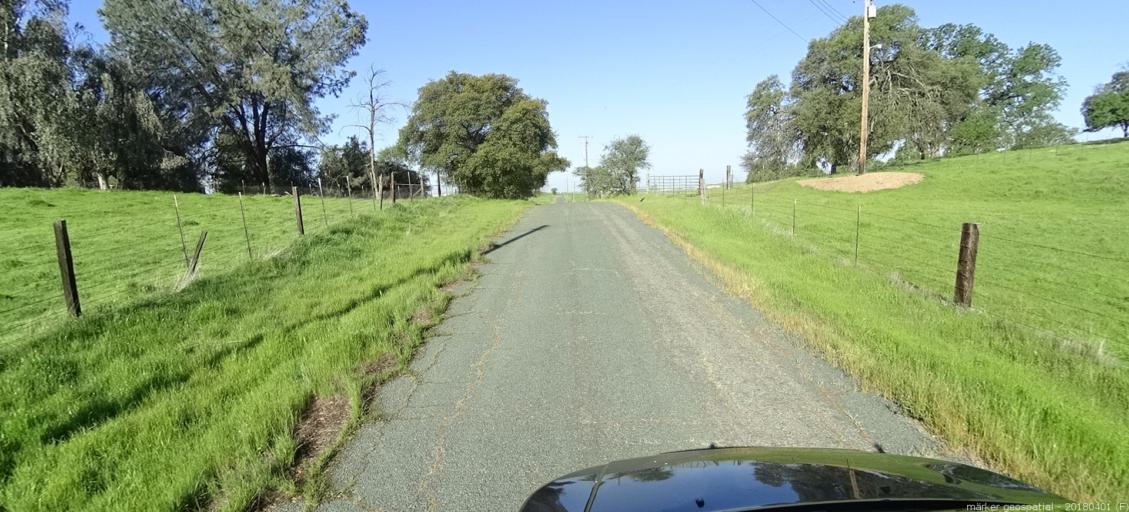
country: US
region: California
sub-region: Sacramento County
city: Rancho Murieta
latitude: 38.4641
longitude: -121.0378
